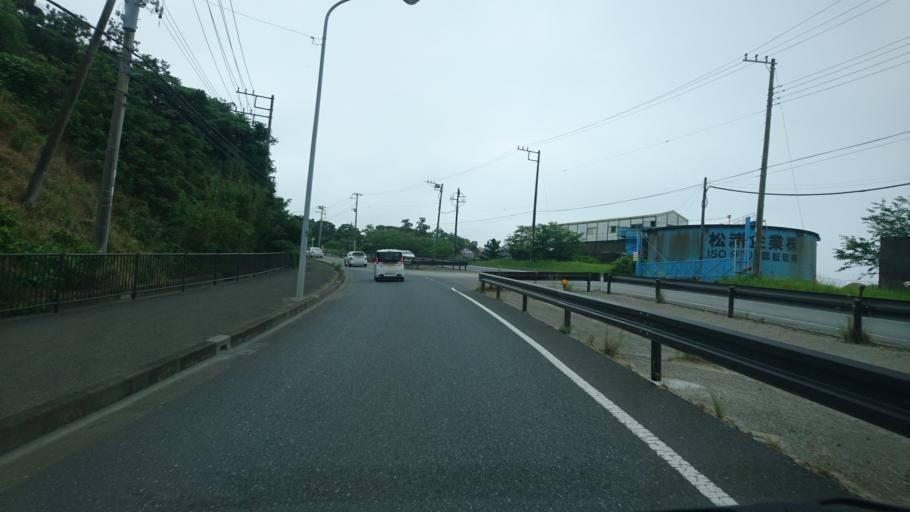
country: JP
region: Chiba
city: Kimitsu
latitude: 35.2456
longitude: 139.8871
